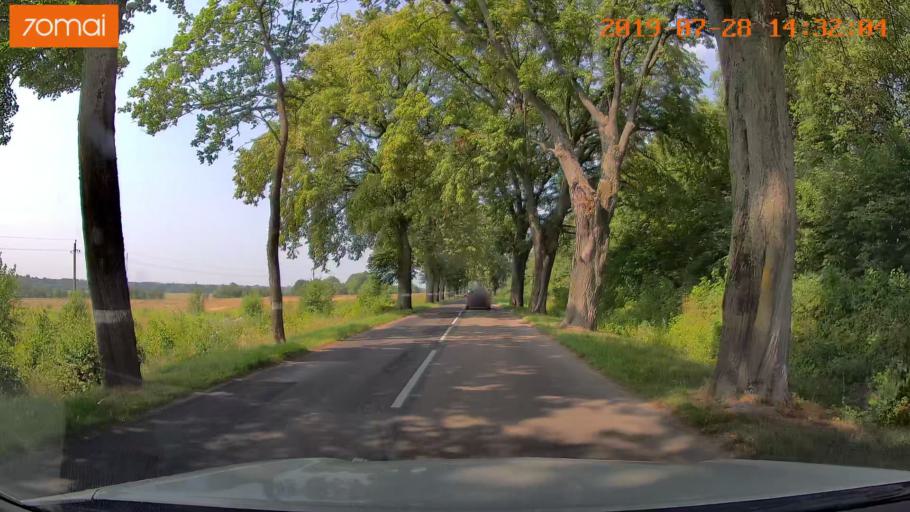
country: RU
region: Kaliningrad
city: Primorsk
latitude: 54.8103
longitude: 20.0453
